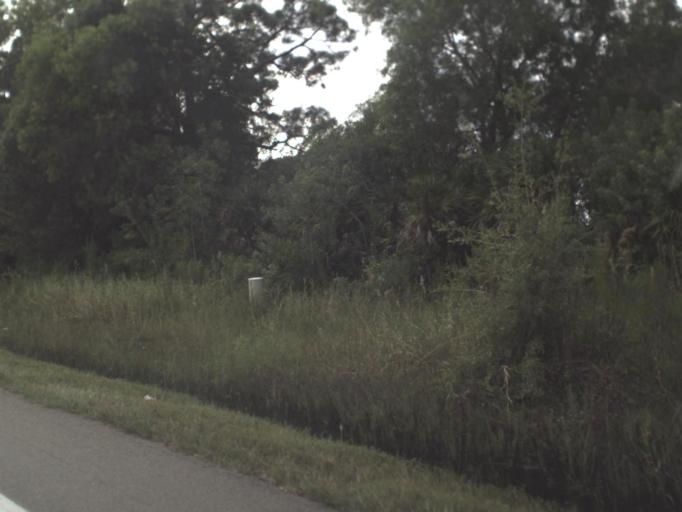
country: US
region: Florida
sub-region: Lee County
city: Fort Myers Shores
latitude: 26.7949
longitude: -81.7605
